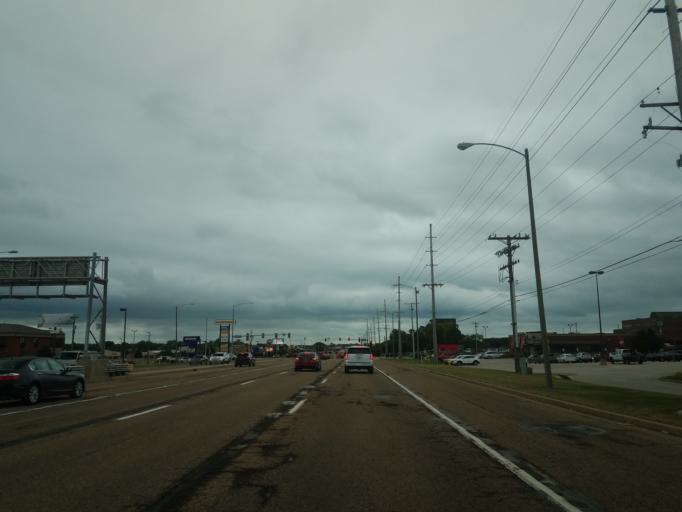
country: US
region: Illinois
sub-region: McLean County
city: Bloomington
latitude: 40.4856
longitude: -88.9529
